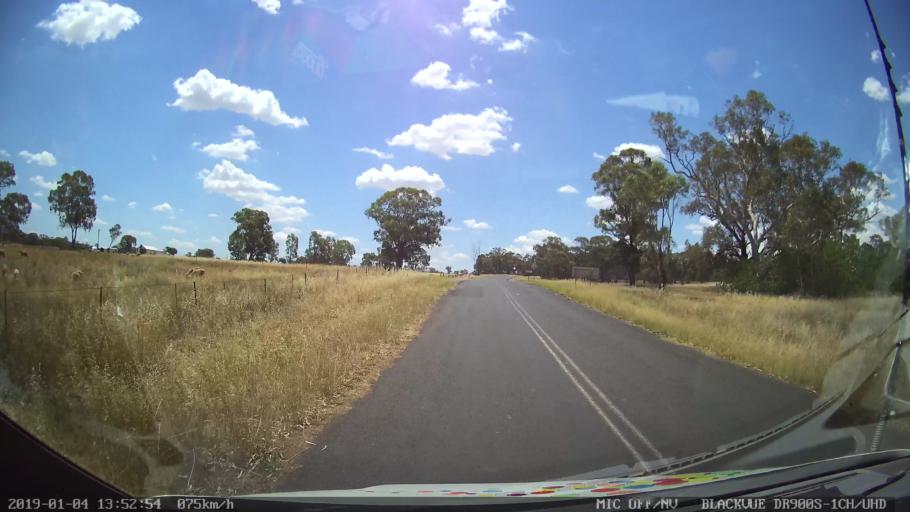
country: AU
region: New South Wales
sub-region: Dubbo Municipality
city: Dubbo
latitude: -32.3889
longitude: 148.5717
